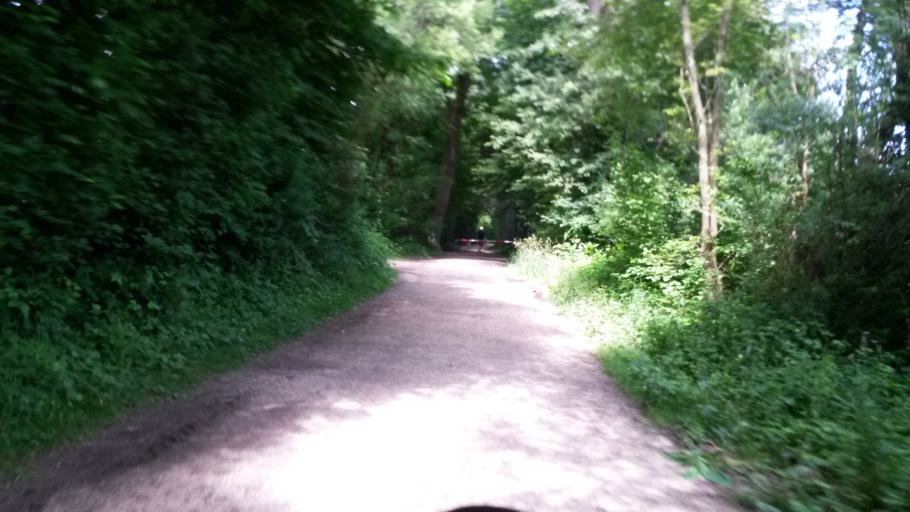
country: DE
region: Bavaria
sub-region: Upper Bavaria
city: Ubersee
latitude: 47.8505
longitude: 12.4760
